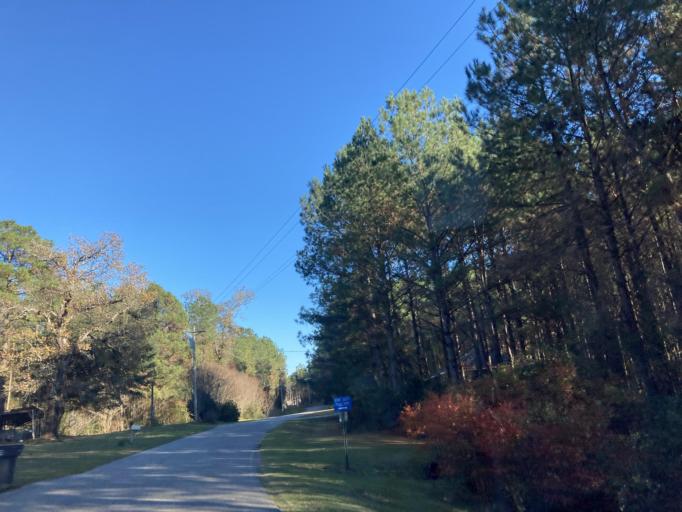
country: US
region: Mississippi
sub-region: Lamar County
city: Sumrall
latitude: 31.3661
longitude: -89.5654
